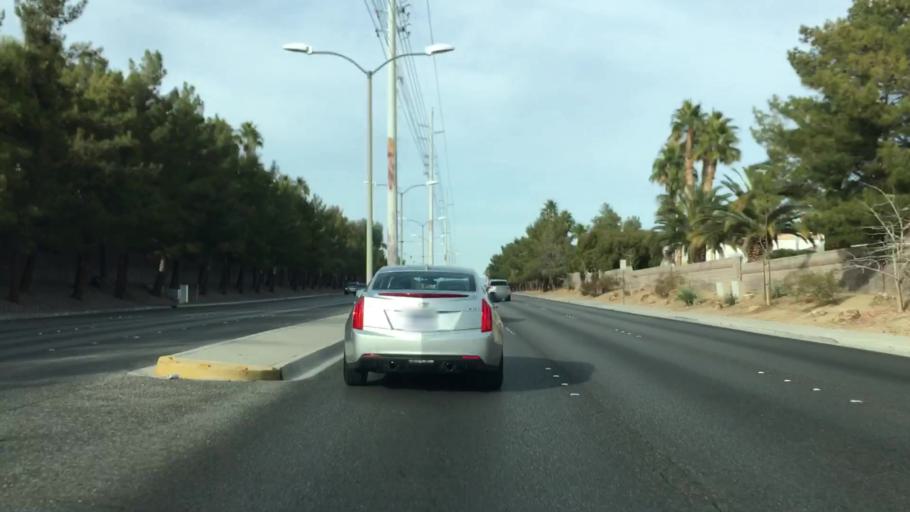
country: US
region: Nevada
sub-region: Clark County
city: Whitney
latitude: 36.0457
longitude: -115.0823
